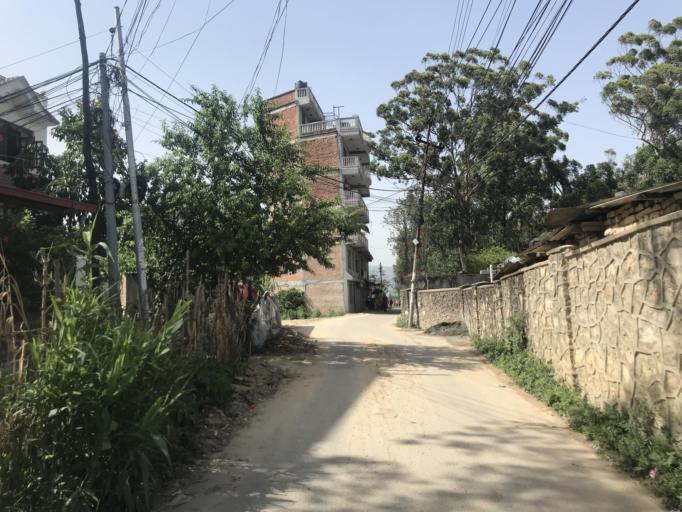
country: NP
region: Central Region
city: Kirtipur
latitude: 27.6801
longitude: 85.2816
